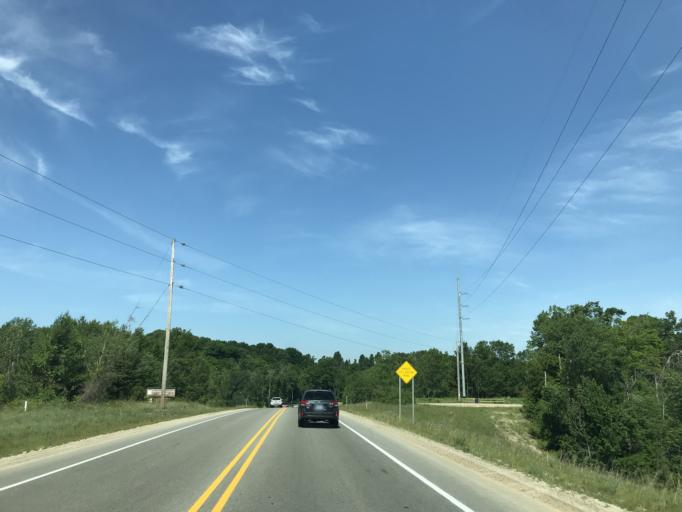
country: US
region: Michigan
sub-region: Grand Traverse County
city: Traverse City
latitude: 44.6982
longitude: -85.6204
